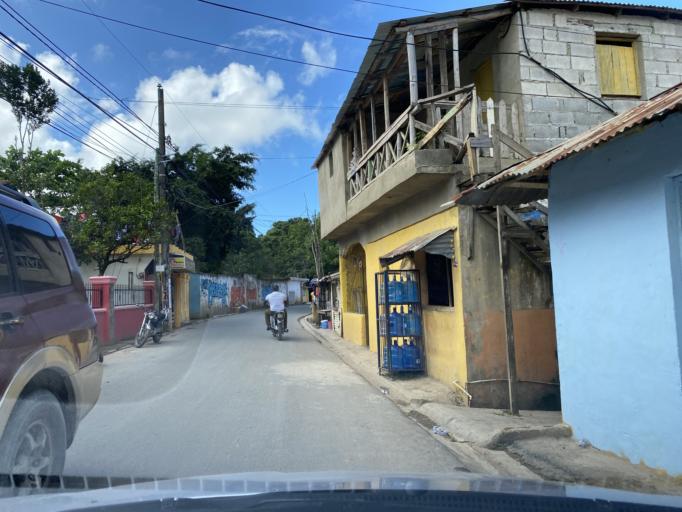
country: DO
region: Samana
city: Las Terrenas
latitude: 19.3068
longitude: -69.5407
